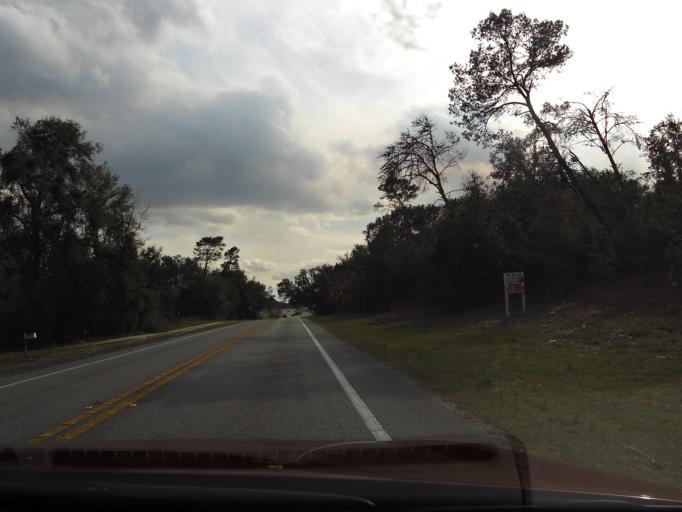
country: US
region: Florida
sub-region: Volusia County
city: De Leon Springs
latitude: 29.1276
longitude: -81.3516
